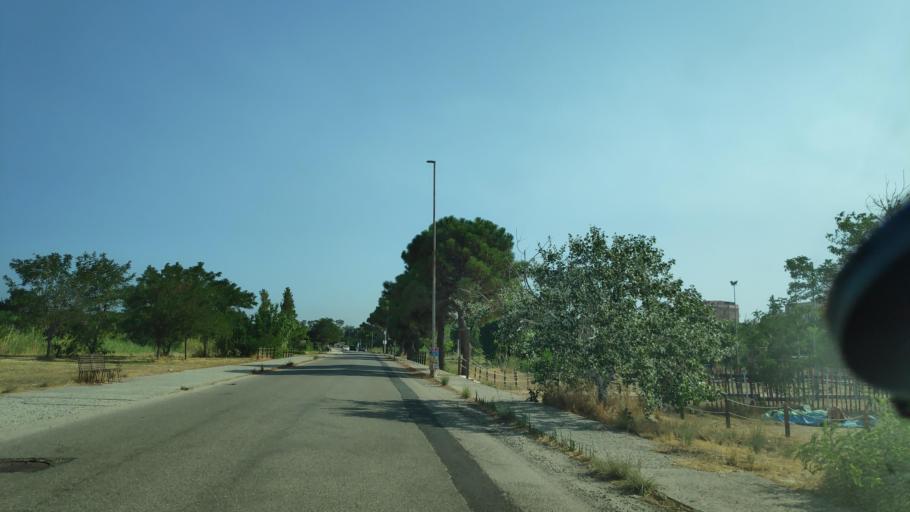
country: IT
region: Calabria
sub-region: Provincia di Catanzaro
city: Badolato Marina
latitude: 38.5745
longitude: 16.5686
